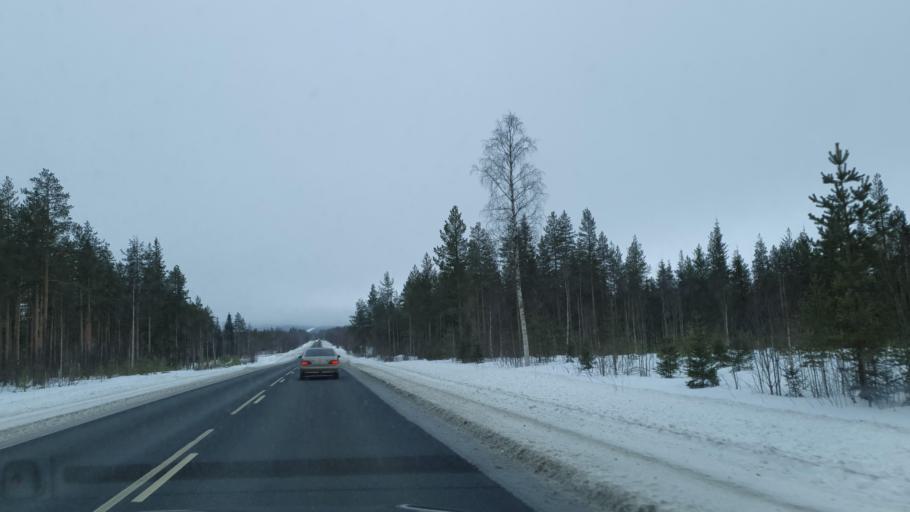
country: FI
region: Lapland
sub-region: Torniolaakso
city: Pello
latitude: 66.7374
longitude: 23.9148
